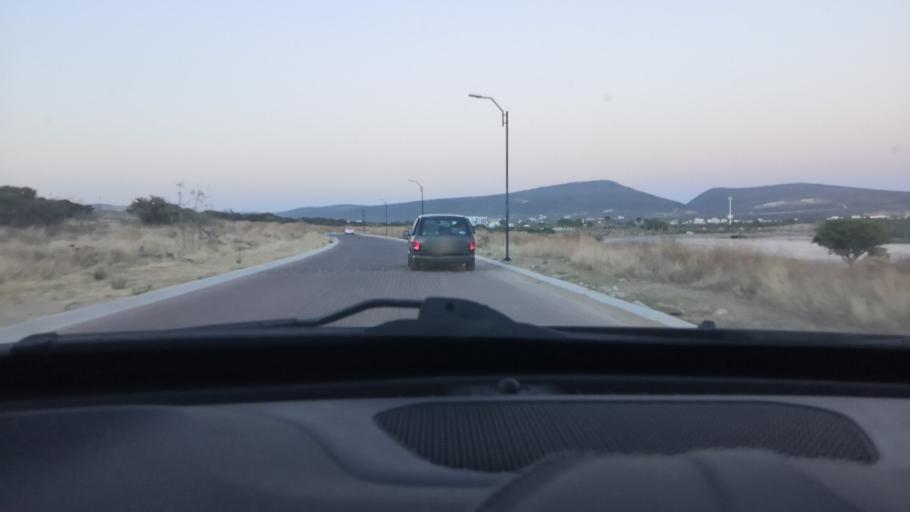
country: MX
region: Guanajuato
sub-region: Leon
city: Fraccionamiento Paseo de las Torres
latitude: 21.2285
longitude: -101.8091
